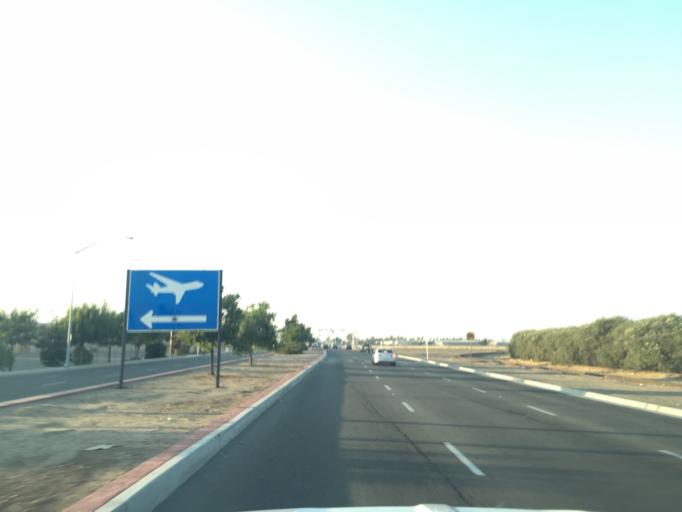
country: US
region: California
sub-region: Fresno County
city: Sunnyside
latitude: 36.7628
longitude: -119.7003
